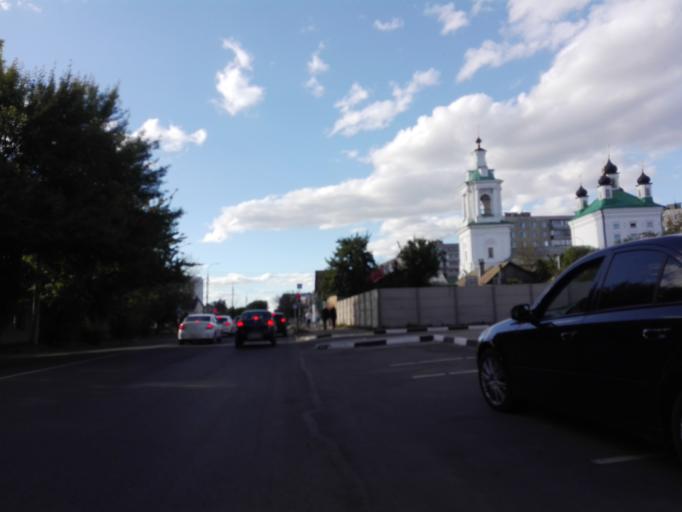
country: RU
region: Orjol
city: Orel
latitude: 52.9532
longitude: 36.0744
